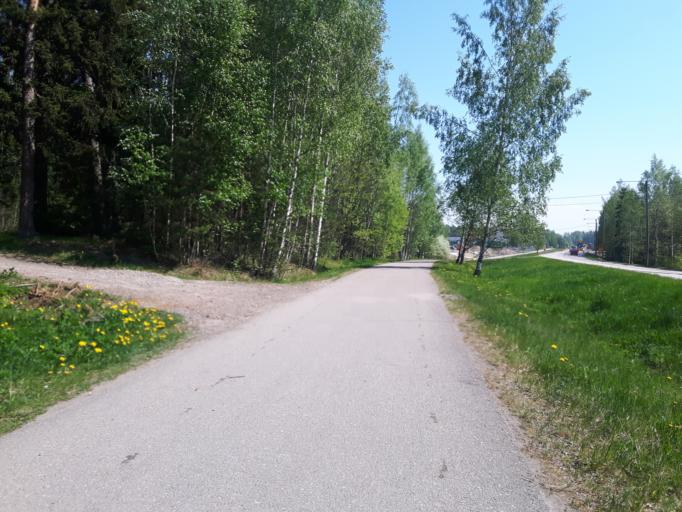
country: FI
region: Uusimaa
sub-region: Helsinki
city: Nickby
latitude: 60.2984
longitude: 25.3343
